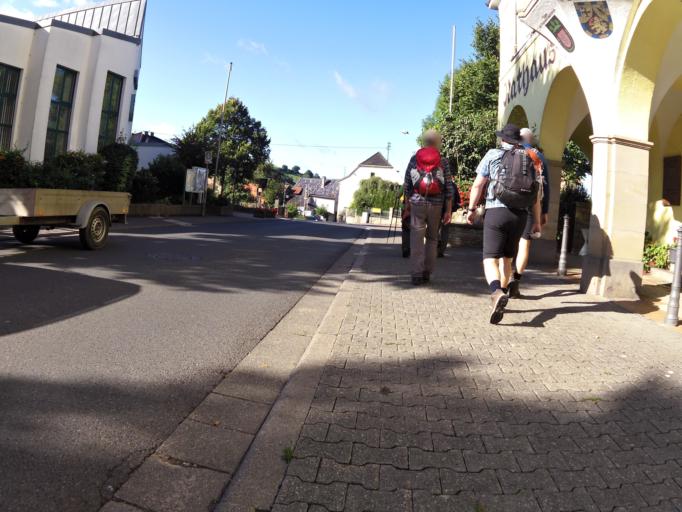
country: DE
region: Rheinland-Pfalz
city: Waldbockelheim
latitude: 49.8178
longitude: 7.7194
